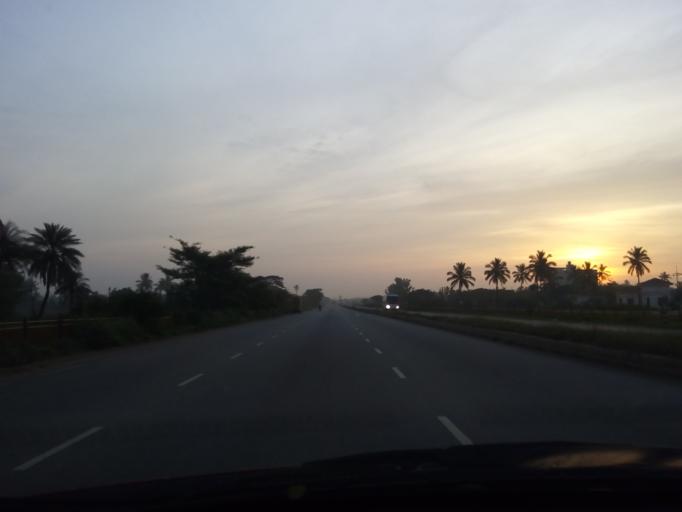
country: IN
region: Karnataka
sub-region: Bangalore Rural
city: Devanhalli
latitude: 13.2336
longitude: 77.6941
